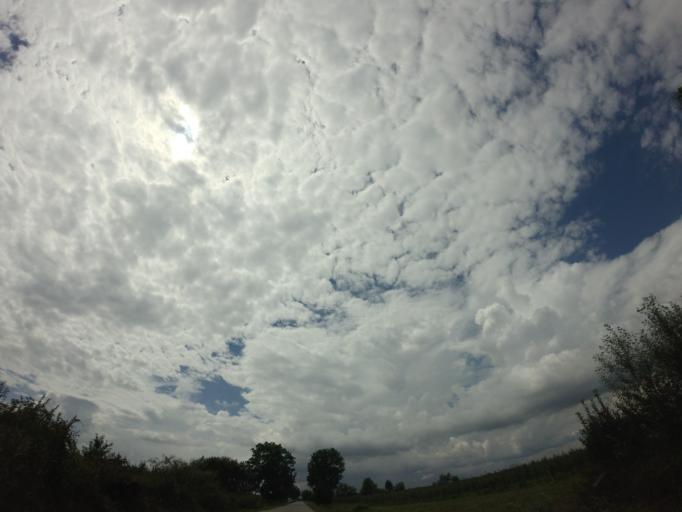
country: PL
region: Lublin Voivodeship
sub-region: Powiat opolski
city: Wilkow
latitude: 51.2421
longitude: 21.8550
